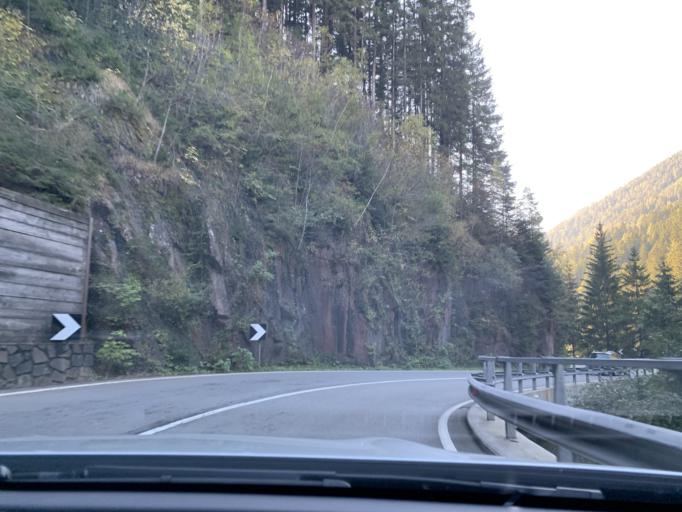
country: IT
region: Trentino-Alto Adige
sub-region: Bolzano
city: Nova Levante
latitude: 46.4257
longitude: 11.5101
